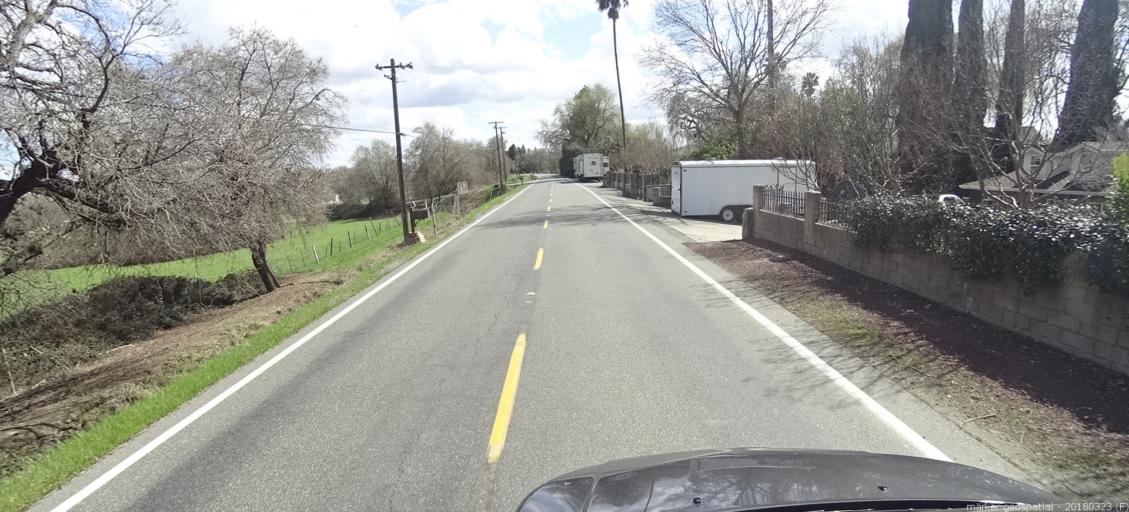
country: US
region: California
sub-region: Yolo County
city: West Sacramento
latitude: 38.6108
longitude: -121.5579
